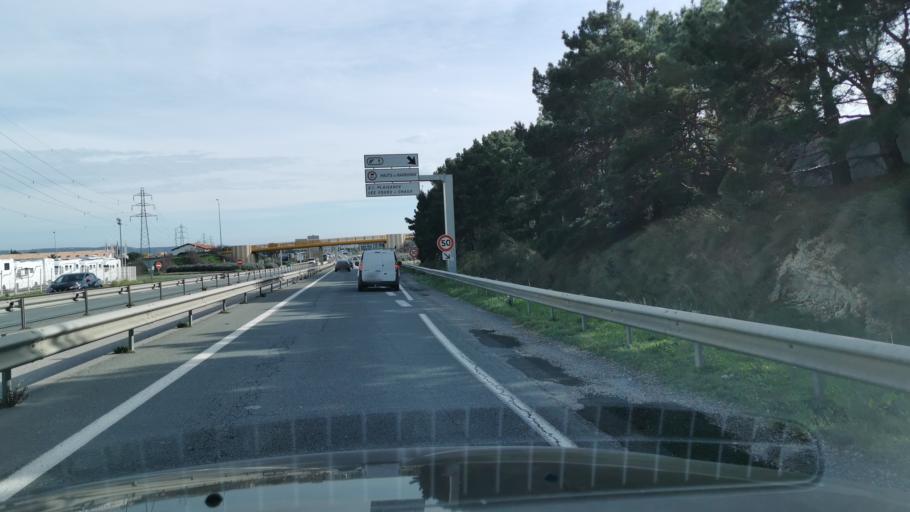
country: FR
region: Languedoc-Roussillon
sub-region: Departement de l'Aude
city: Narbonne
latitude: 43.1695
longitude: 2.9805
